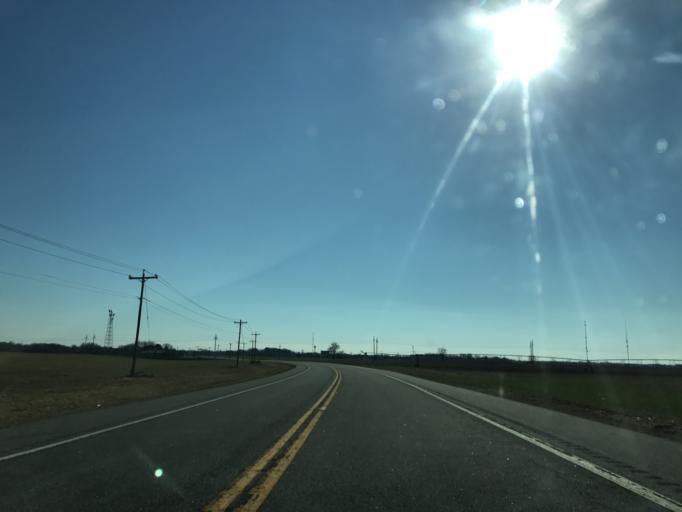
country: US
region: Maryland
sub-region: Queen Anne's County
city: Centreville
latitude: 38.9671
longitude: -76.0766
